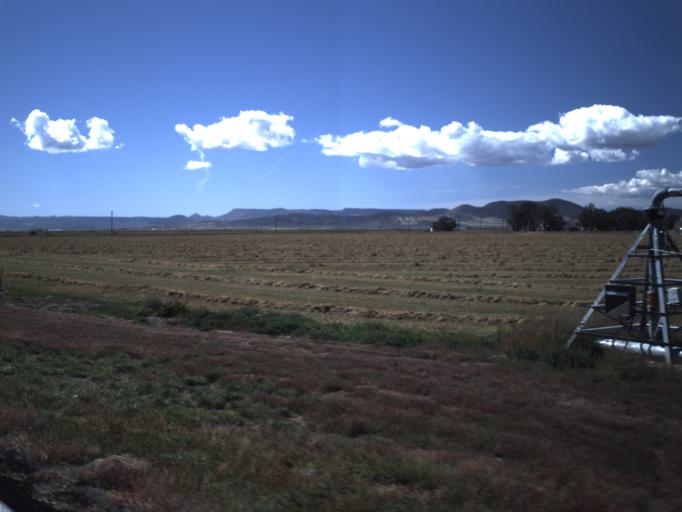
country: US
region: Utah
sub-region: Washington County
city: Enterprise
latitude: 37.6961
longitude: -113.6565
